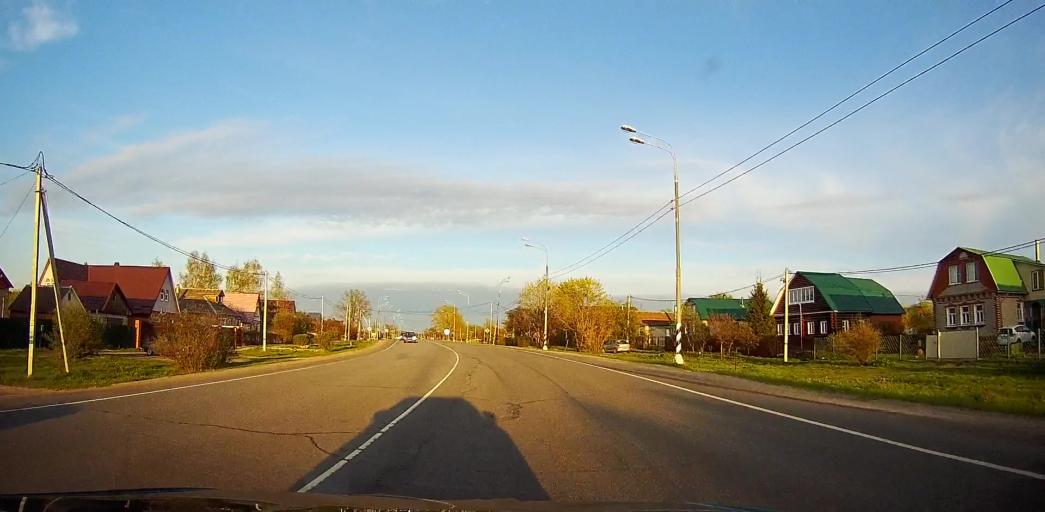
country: RU
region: Moskovskaya
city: Troitskoye
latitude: 55.2254
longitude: 38.5624
